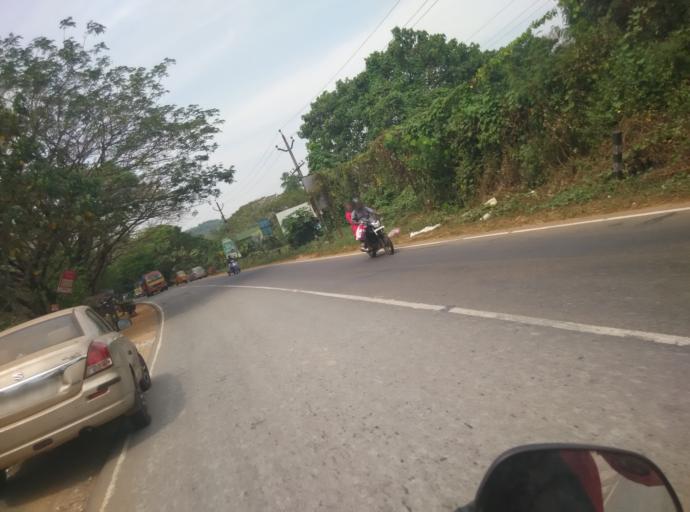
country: IN
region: Kerala
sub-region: Kottayam
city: Lalam
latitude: 9.7036
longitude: 76.6628
